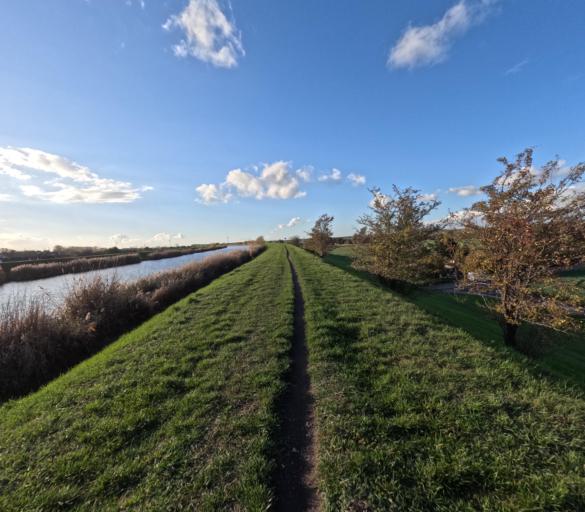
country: DE
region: Saxony
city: Schkeuditz
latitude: 51.3578
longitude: 12.2208
